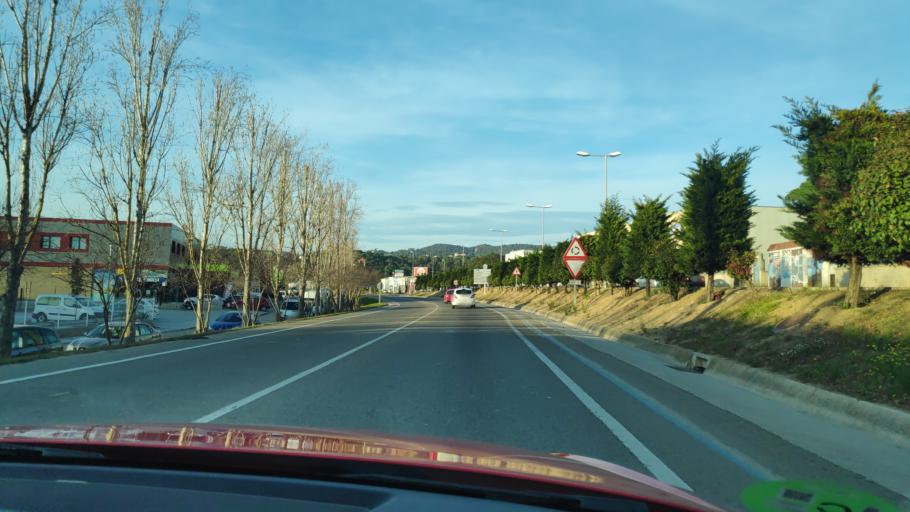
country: ES
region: Catalonia
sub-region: Provincia de Girona
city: Lloret de Mar
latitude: 41.7125
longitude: 2.8317
